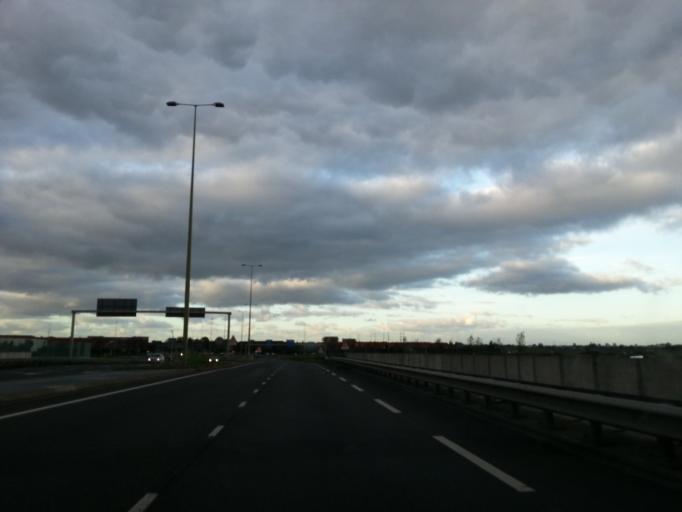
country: NL
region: South Holland
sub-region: Gemeente Lansingerland
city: Berkel en Rodenrijs
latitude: 51.9979
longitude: 4.4523
